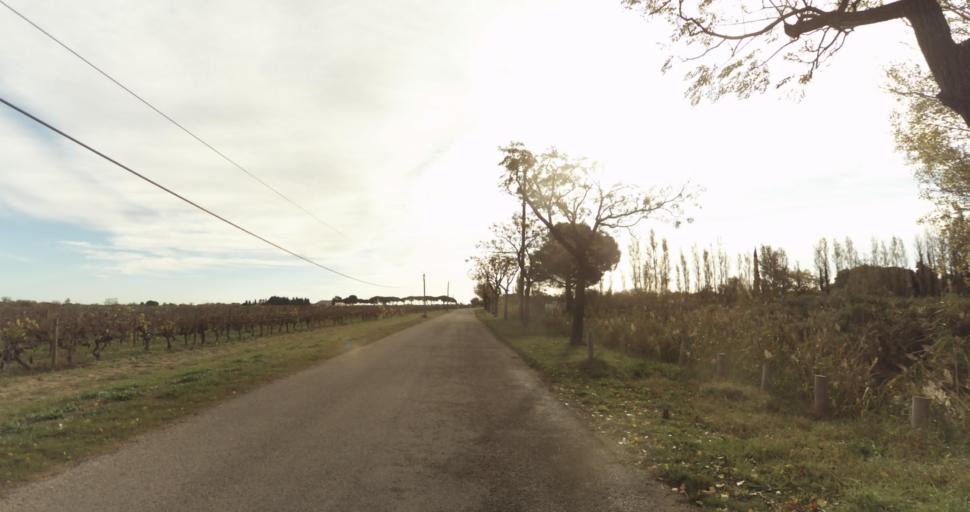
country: FR
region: Languedoc-Roussillon
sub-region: Departement du Gard
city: Aigues-Mortes
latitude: 43.5645
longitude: 4.2092
